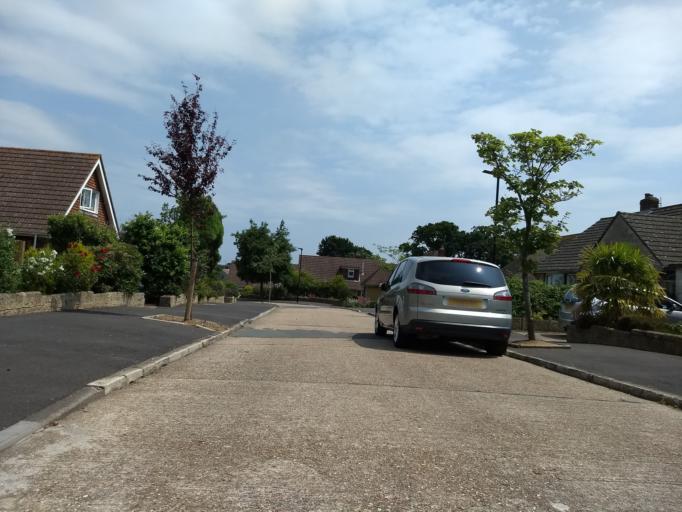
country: GB
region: England
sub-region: Isle of Wight
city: Seaview
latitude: 50.7163
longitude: -1.1299
